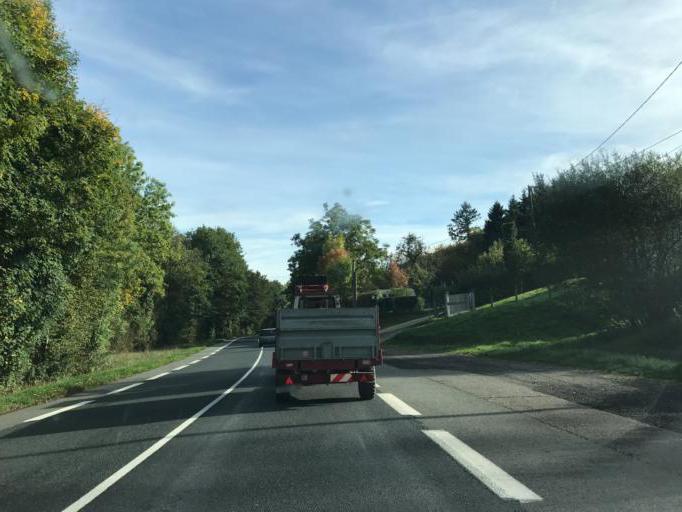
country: FR
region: Rhone-Alpes
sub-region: Departement du Rhone
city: Grandris
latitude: 46.0423
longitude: 4.4887
